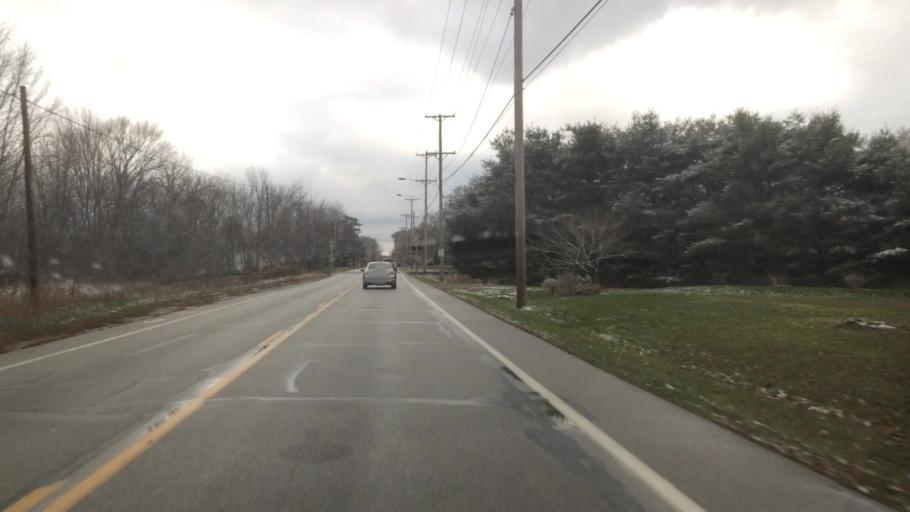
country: US
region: Ohio
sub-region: Summit County
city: Hudson
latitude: 41.2229
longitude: -81.4112
